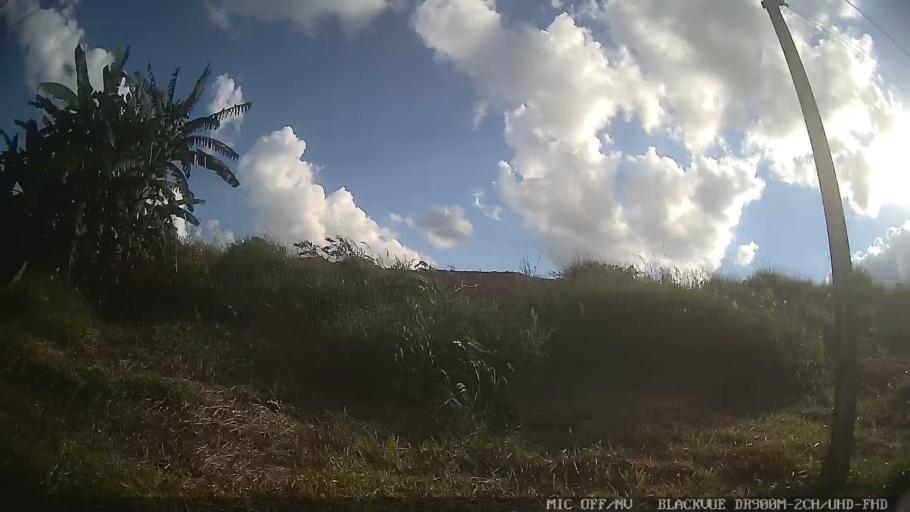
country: BR
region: Minas Gerais
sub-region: Extrema
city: Extrema
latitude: -22.8440
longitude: -46.3260
